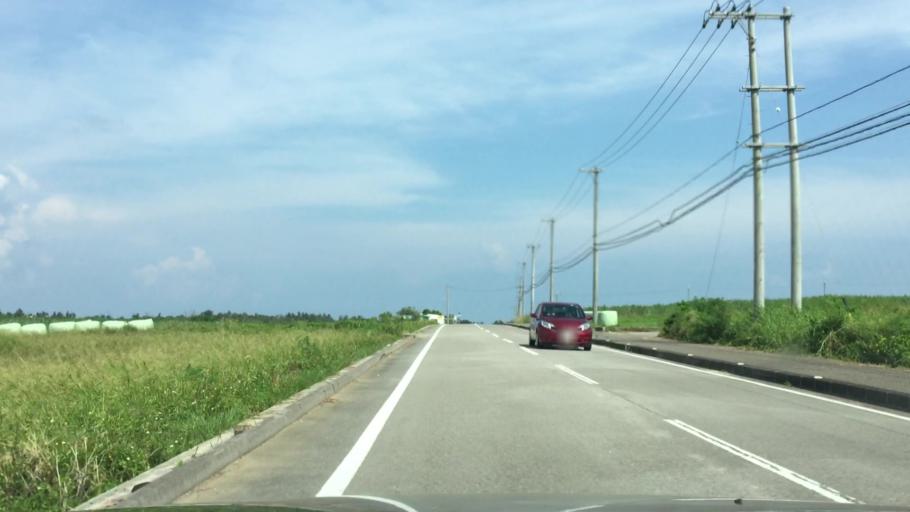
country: JP
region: Okinawa
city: Ishigaki
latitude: 24.5060
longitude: 124.2723
